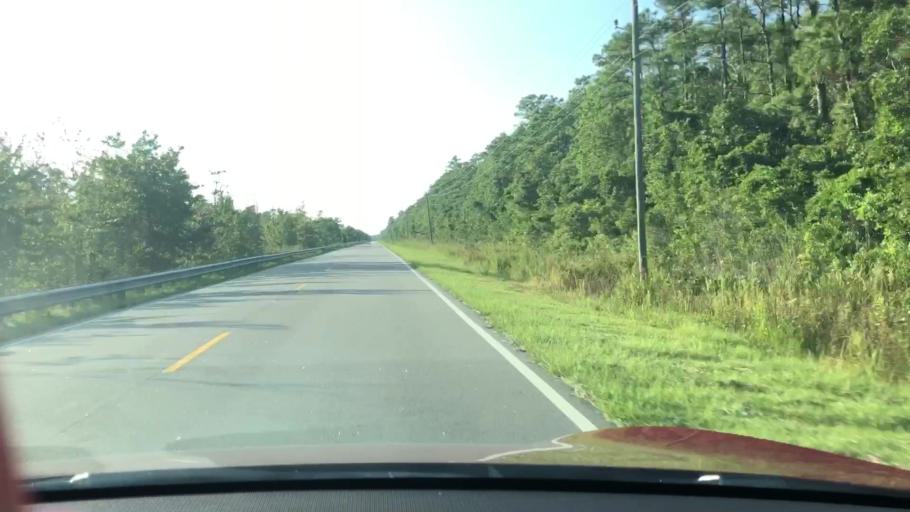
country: US
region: North Carolina
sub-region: Dare County
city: Manteo
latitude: 35.8146
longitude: -75.7944
